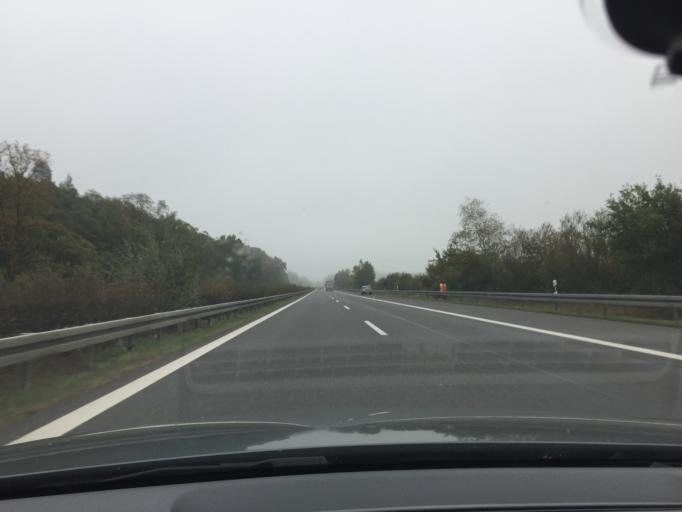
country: DE
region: Brandenburg
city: Bronkow
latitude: 51.6270
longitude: 13.9431
